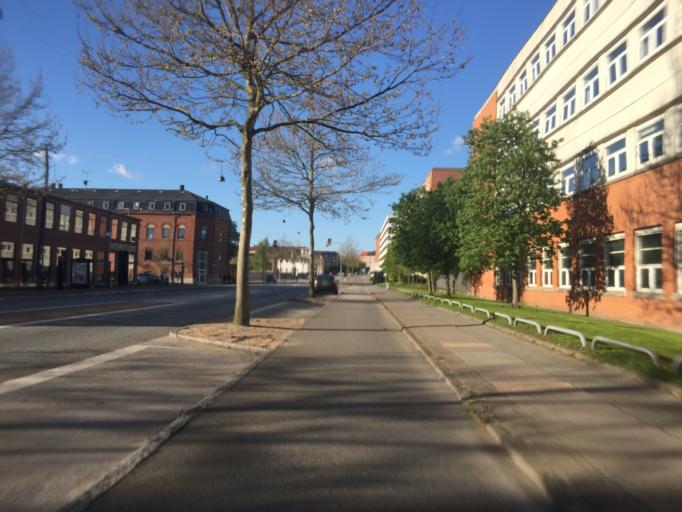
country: DK
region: Capital Region
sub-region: Frederiksberg Kommune
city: Frederiksberg
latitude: 55.6578
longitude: 12.5138
